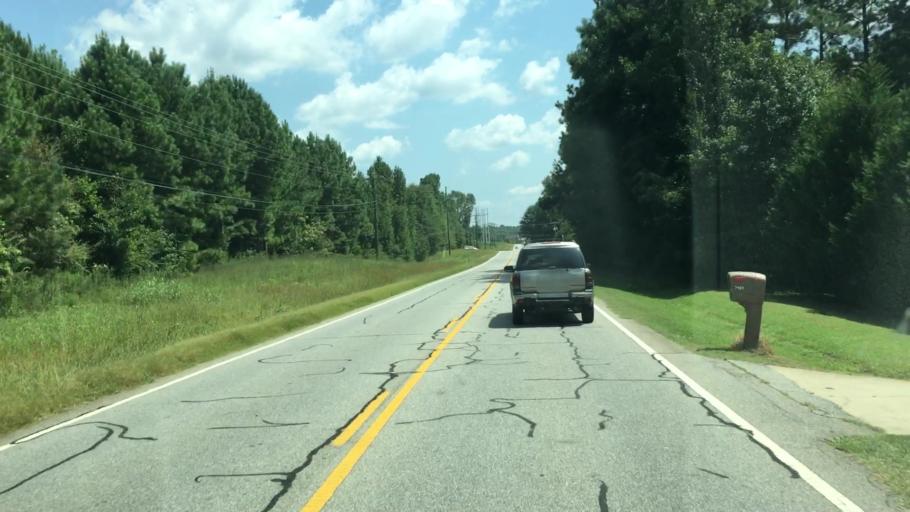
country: US
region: Georgia
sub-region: Barrow County
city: Statham
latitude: 33.9060
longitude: -83.5821
